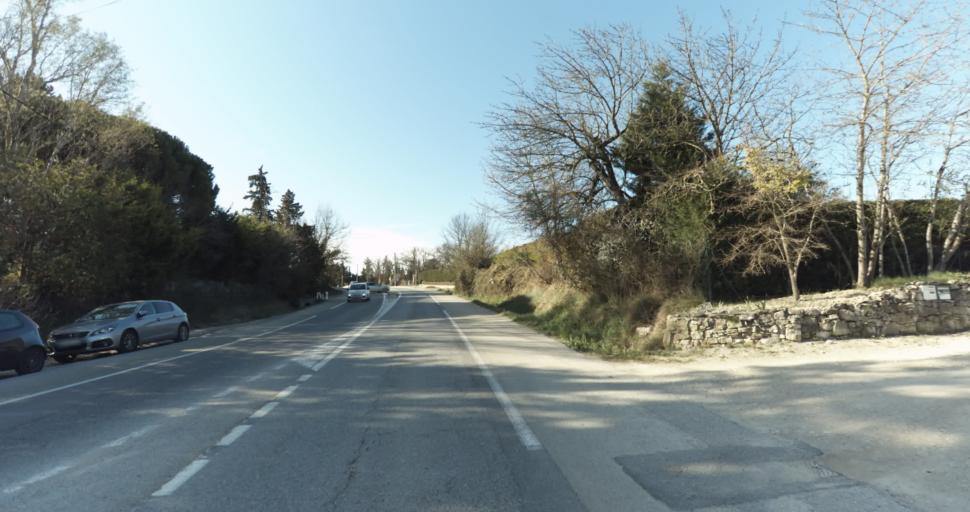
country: FR
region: Provence-Alpes-Cote d'Azur
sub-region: Departement des Bouches-du-Rhone
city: Aix-en-Provence
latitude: 43.5619
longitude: 5.4338
